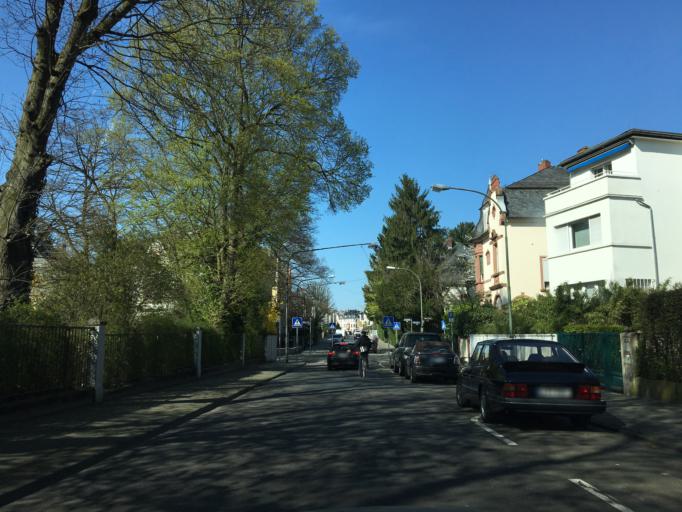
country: DE
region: Hesse
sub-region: Regierungsbezirk Darmstadt
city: Frankfurt am Main
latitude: 50.1526
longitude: 8.6573
